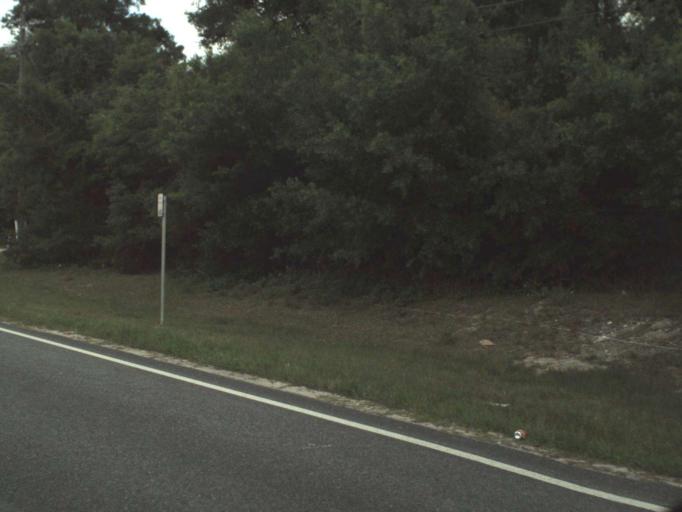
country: US
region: Florida
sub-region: Seminole County
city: Heathrow
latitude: 28.8114
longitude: -81.3573
